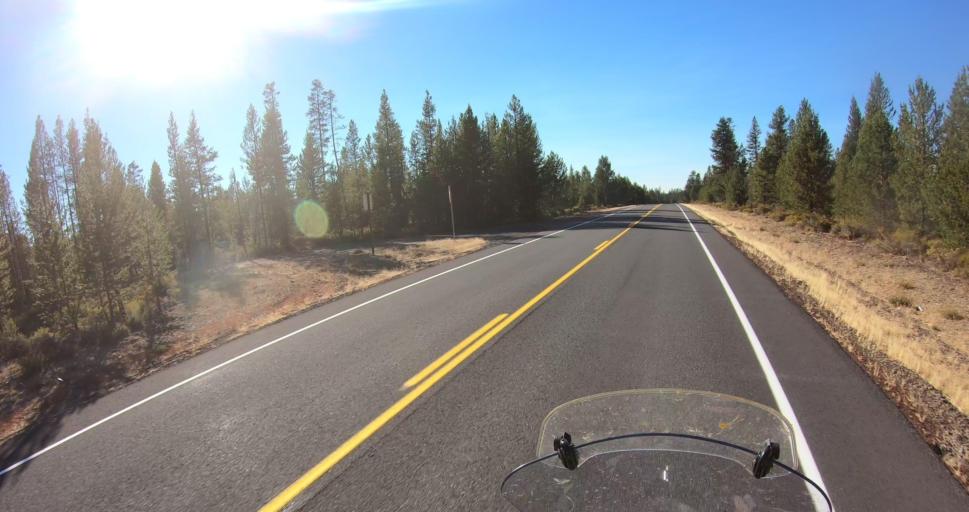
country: US
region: Oregon
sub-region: Deschutes County
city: La Pine
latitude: 43.4520
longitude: -121.3657
